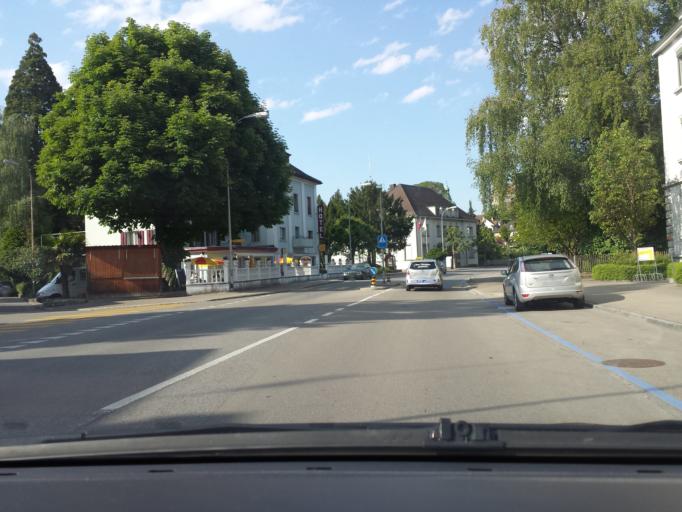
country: CH
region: Thurgau
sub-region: Arbon District
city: Arbon
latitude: 47.5131
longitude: 9.4341
